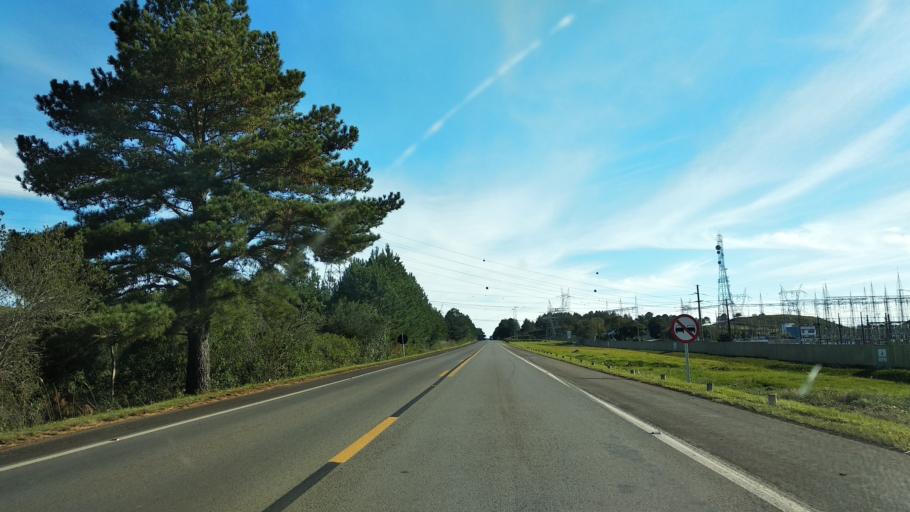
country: BR
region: Santa Catarina
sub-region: Celso Ramos
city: Celso Ramos
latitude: -27.5401
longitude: -51.4127
